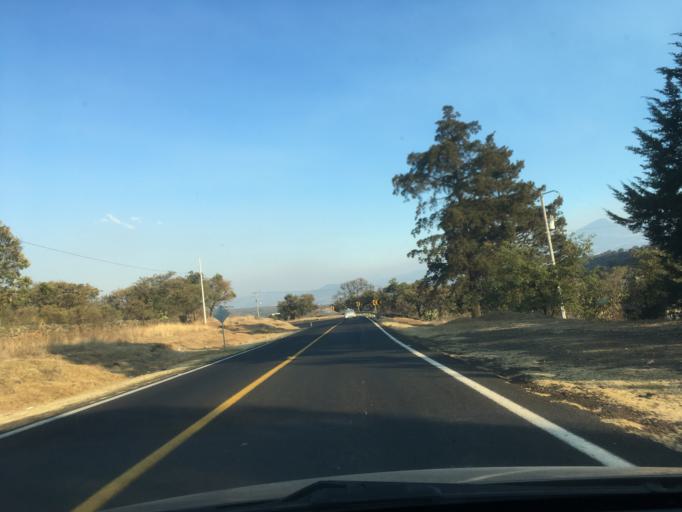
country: MX
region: Michoacan
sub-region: Morelia
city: Iratzio
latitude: 19.6299
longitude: -101.4410
